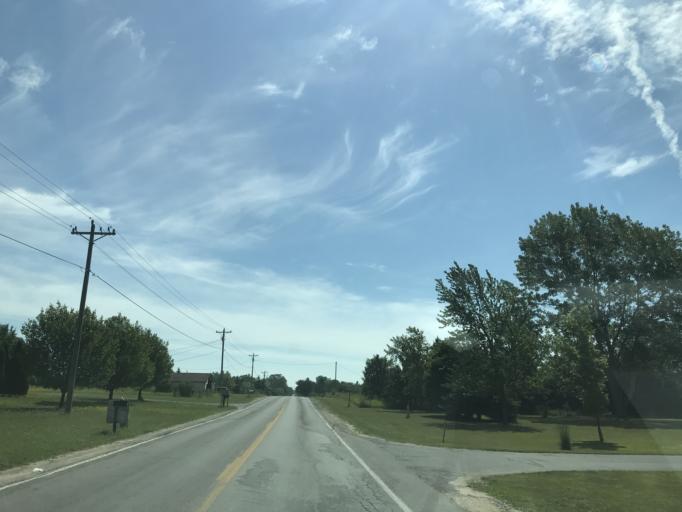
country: US
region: Michigan
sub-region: Grand Traverse County
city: Traverse City
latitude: 44.6575
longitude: -85.6760
